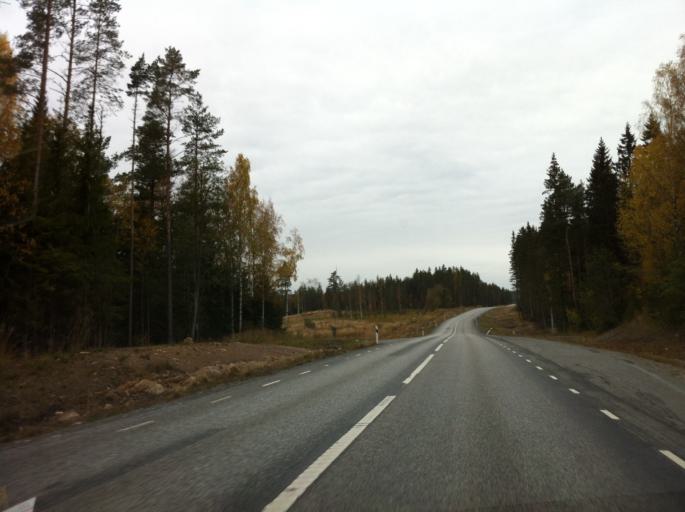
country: SE
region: OErebro
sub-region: Ljusnarsbergs Kommun
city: Kopparberg
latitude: 59.9690
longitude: 15.0196
